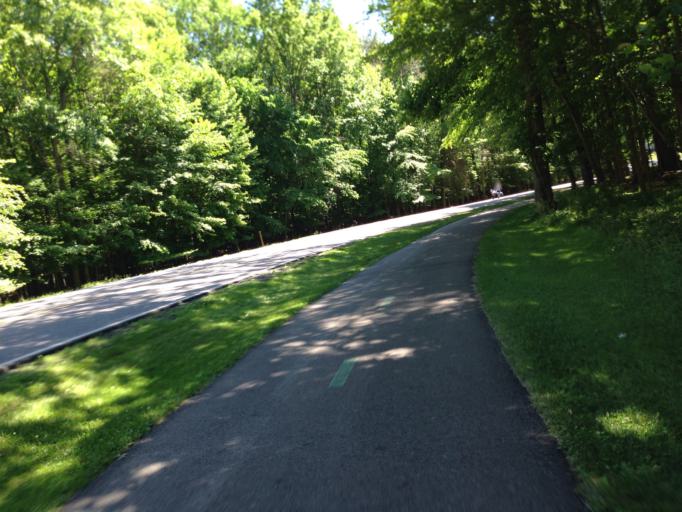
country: US
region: Ohio
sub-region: Cuyahoga County
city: Middleburg Heights
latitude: 41.3449
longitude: -81.8344
